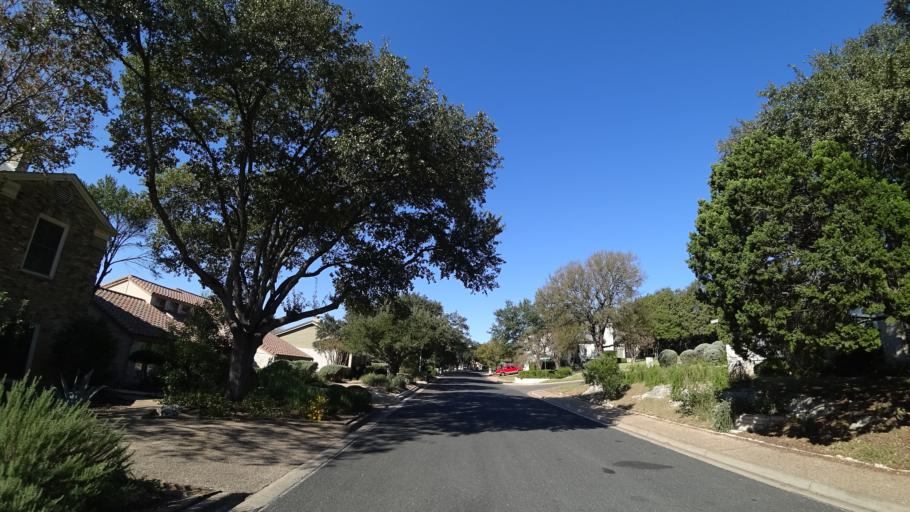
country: US
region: Texas
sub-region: Williamson County
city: Jollyville
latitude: 30.4062
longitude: -97.7624
